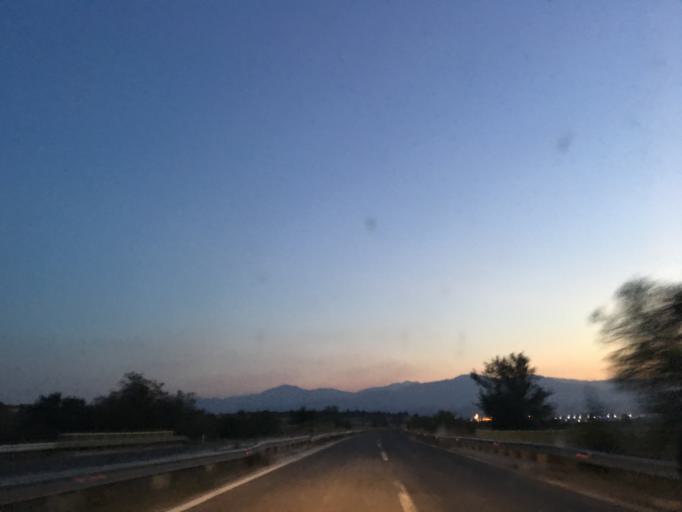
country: MK
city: Miladinovci
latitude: 41.9743
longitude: 21.6493
